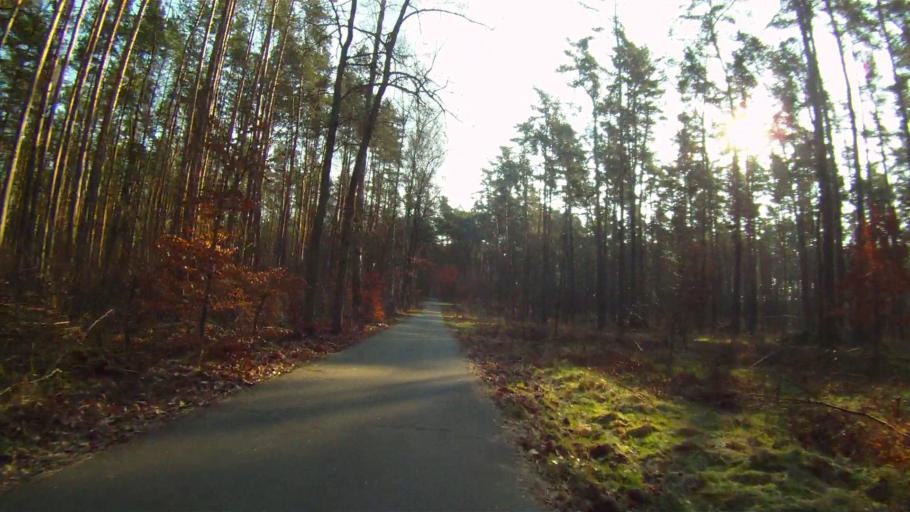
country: DE
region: Berlin
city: Rahnsdorf
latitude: 52.4187
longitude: 13.7151
